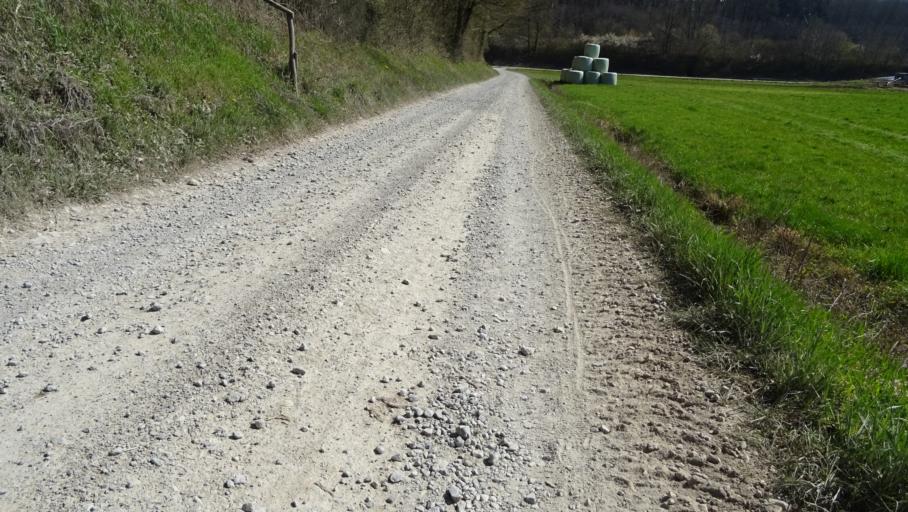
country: DE
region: Baden-Wuerttemberg
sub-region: Karlsruhe Region
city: Limbach
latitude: 49.4150
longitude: 9.2391
